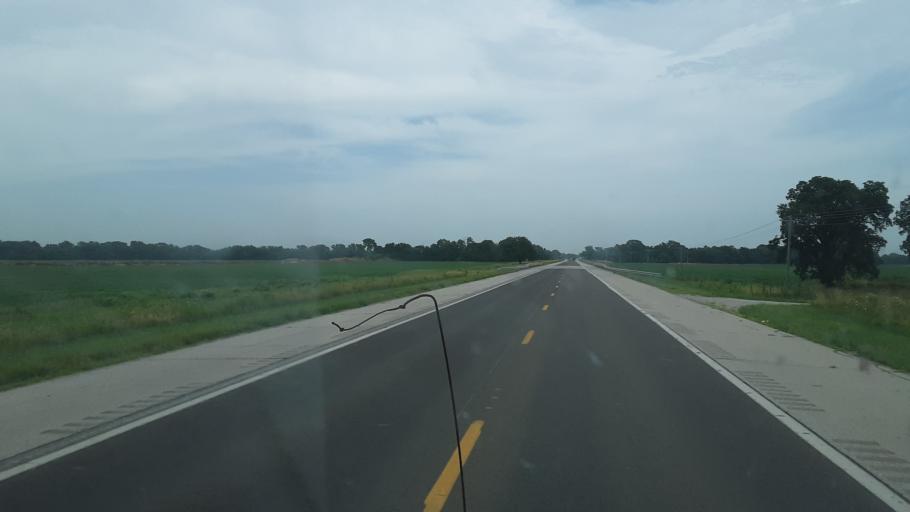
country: US
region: Kansas
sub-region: Allen County
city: Iola
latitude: 37.9219
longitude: -95.4372
